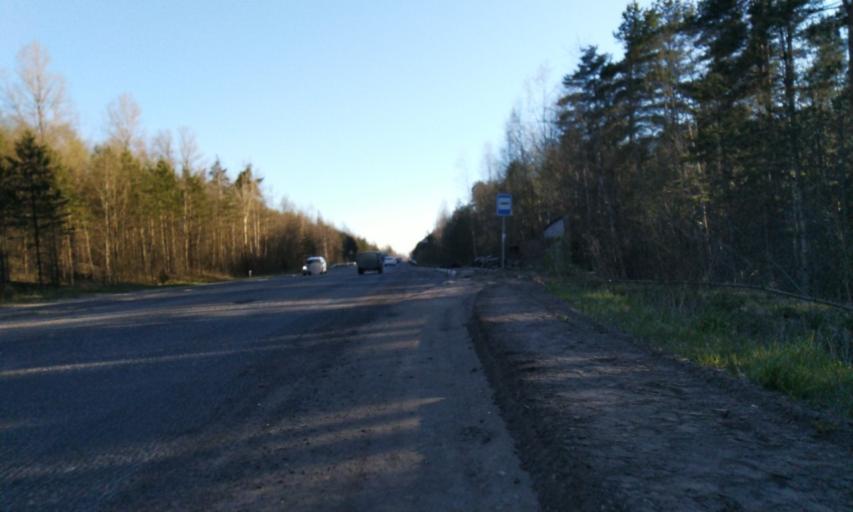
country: RU
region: Leningrad
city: Toksovo
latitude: 60.1280
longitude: 30.5181
